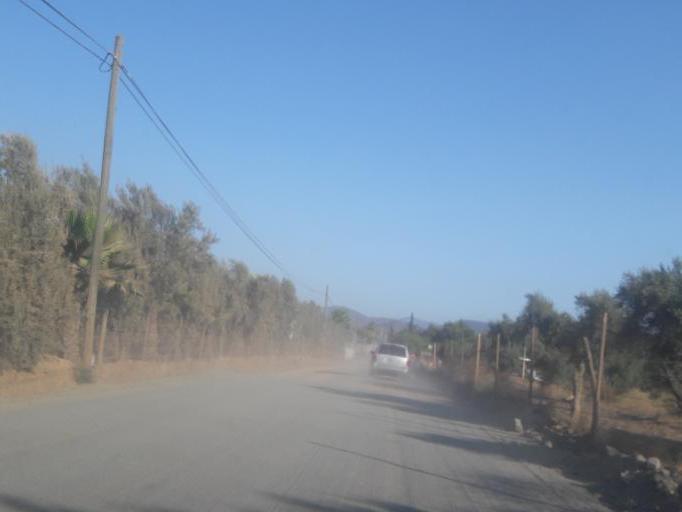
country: MX
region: Baja California
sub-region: Ensenada
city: Rancho Verde
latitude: 32.0819
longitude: -116.6226
